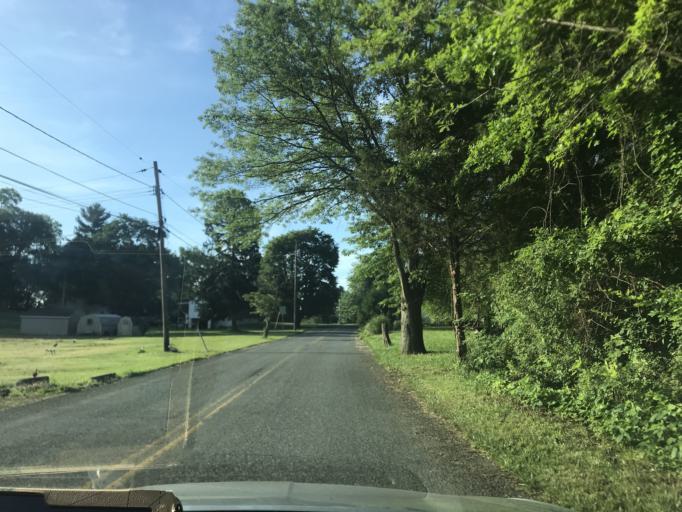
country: US
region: Maryland
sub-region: Harford County
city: South Bel Air
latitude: 39.6063
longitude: -76.3043
